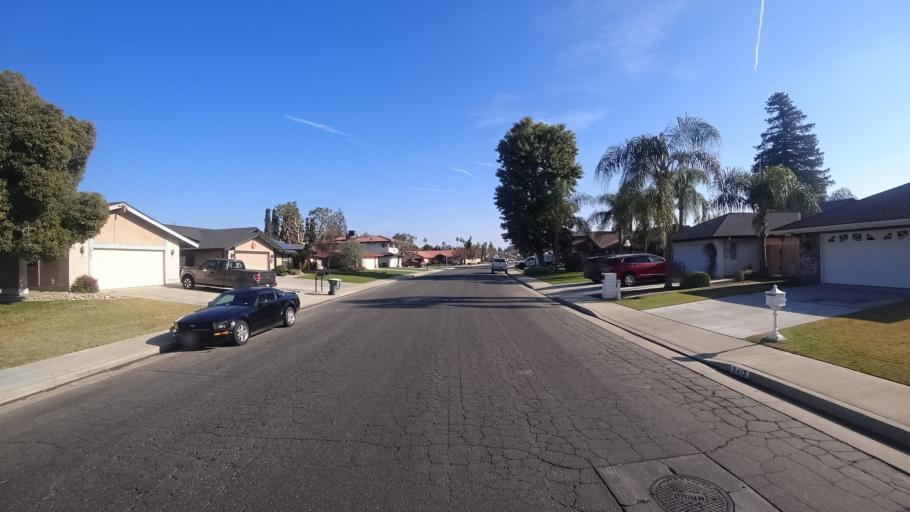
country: US
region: California
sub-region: Kern County
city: Greenacres
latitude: 35.3236
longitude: -119.1071
